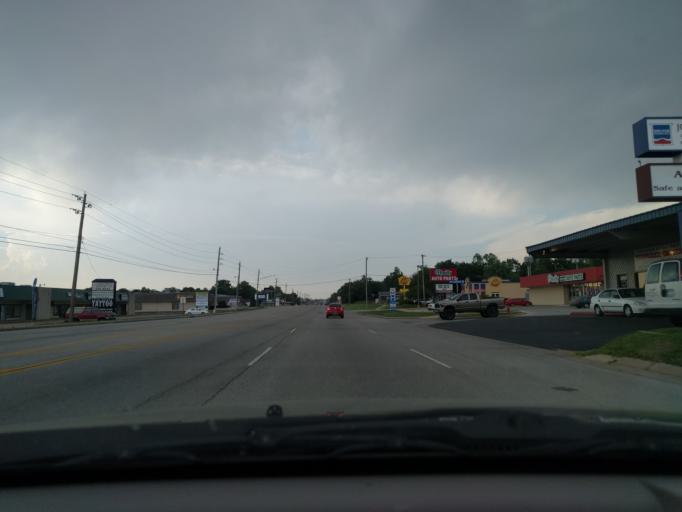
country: US
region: Oklahoma
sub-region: Tulsa County
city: Broken Arrow
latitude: 36.0470
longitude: -95.7974
